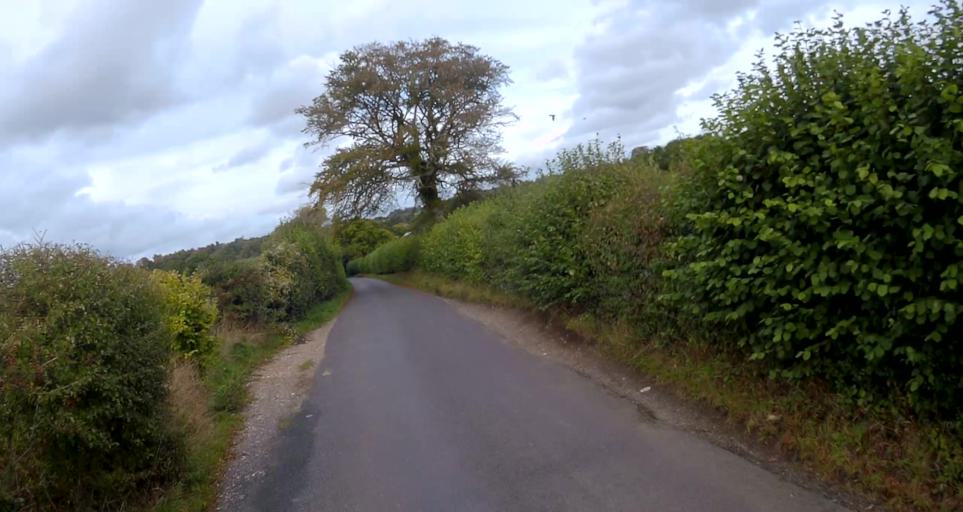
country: GB
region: England
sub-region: Hampshire
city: Four Marks
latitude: 51.1184
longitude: -1.0943
